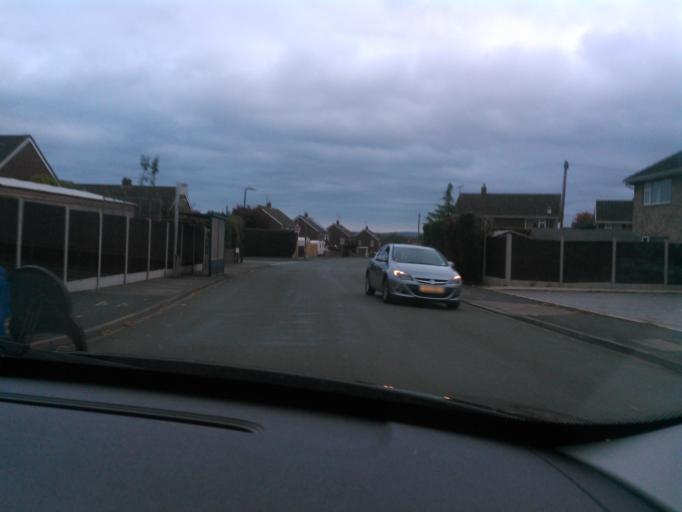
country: GB
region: England
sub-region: Shropshire
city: Shrewsbury
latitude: 52.7370
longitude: -2.7452
